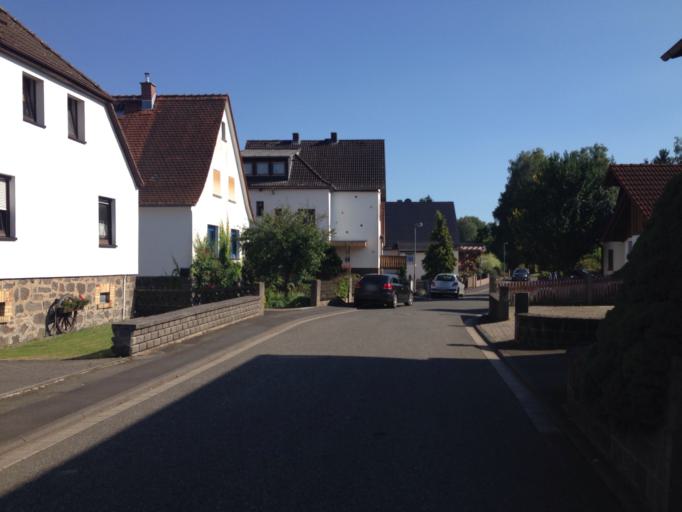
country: DE
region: Hesse
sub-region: Regierungsbezirk Giessen
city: Rabenau
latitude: 50.6591
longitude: 8.8907
